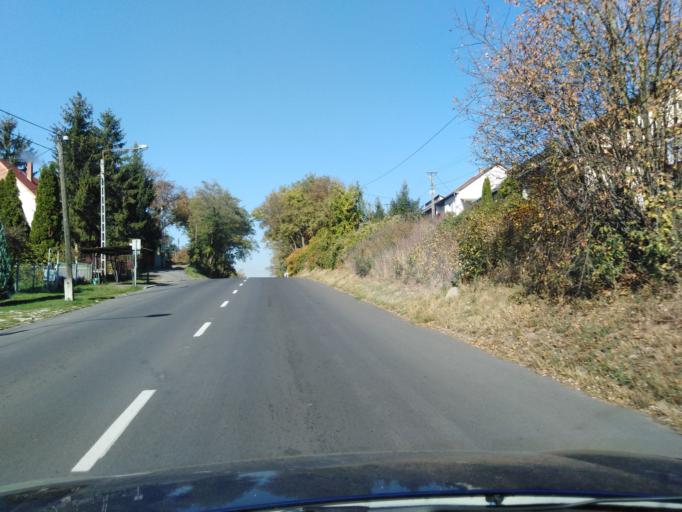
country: HU
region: Nograd
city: Salgotarjan
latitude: 48.1123
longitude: 19.7852
